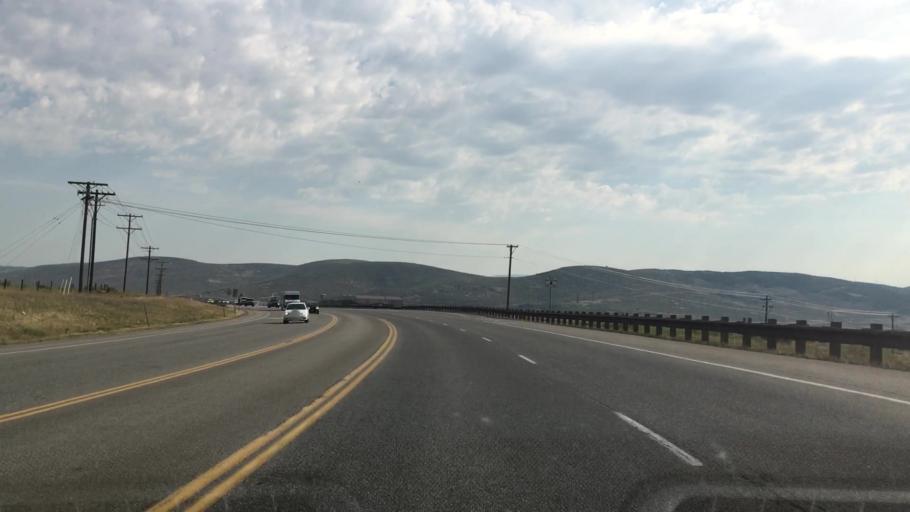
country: US
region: Utah
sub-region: Summit County
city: Park City
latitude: 40.6730
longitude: -111.4697
